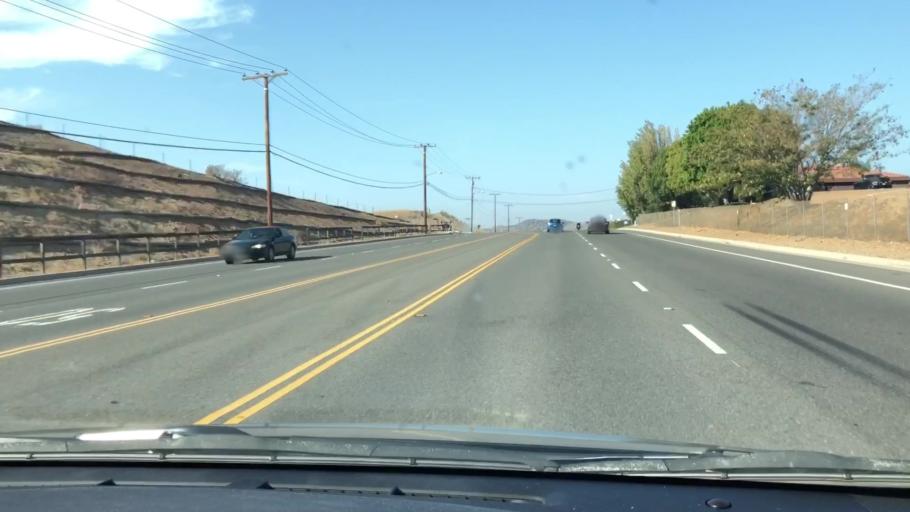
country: US
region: California
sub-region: Orange County
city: Villa Park
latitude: 33.8029
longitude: -117.7690
